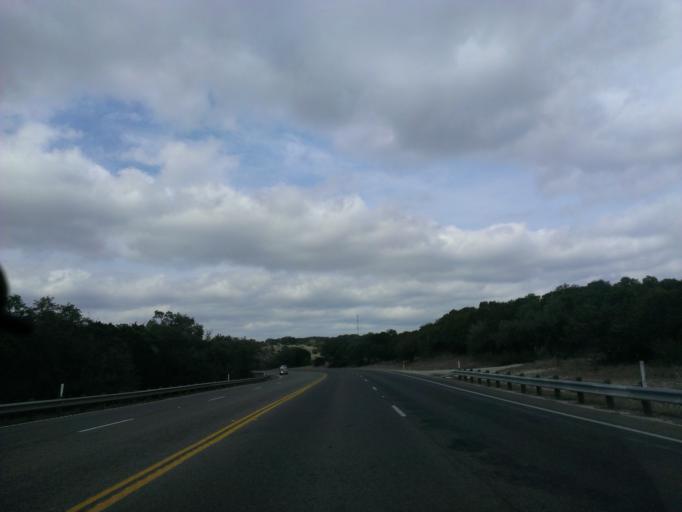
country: US
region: Texas
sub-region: Travis County
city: Briarcliff
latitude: 30.4231
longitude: -98.1286
